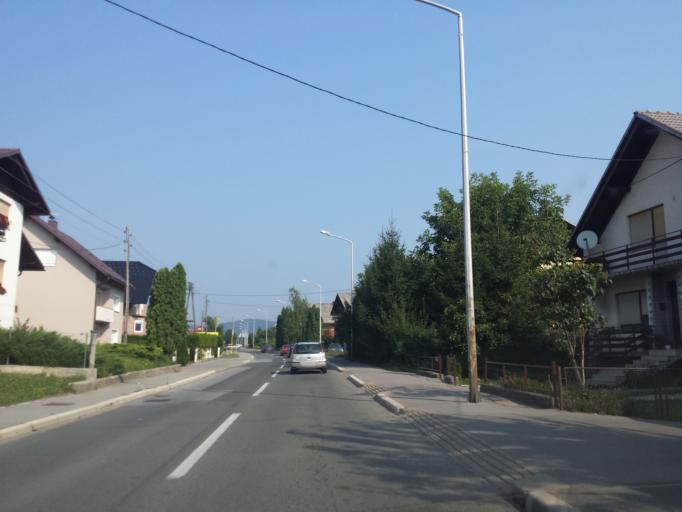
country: HR
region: Karlovacka
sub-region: Grad Ogulin
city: Ogulin
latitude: 45.2494
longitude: 15.2420
